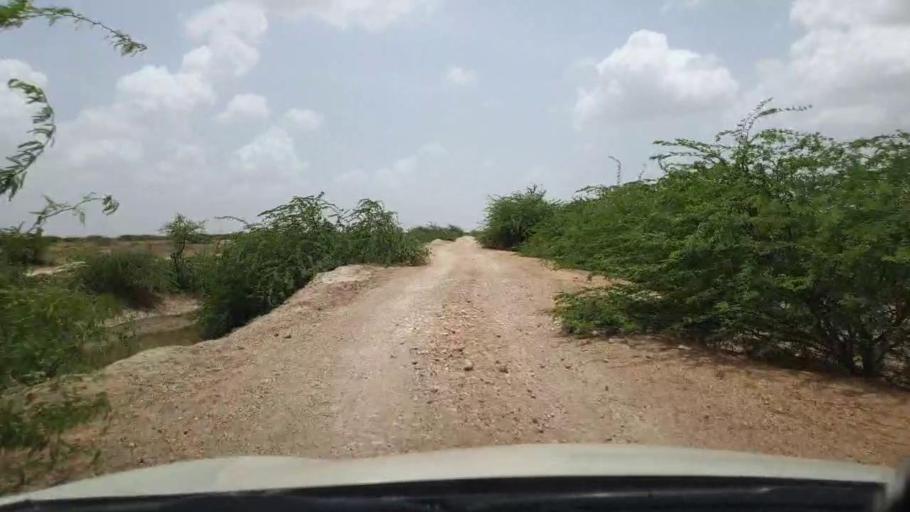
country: PK
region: Sindh
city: Kadhan
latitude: 24.3579
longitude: 68.9251
